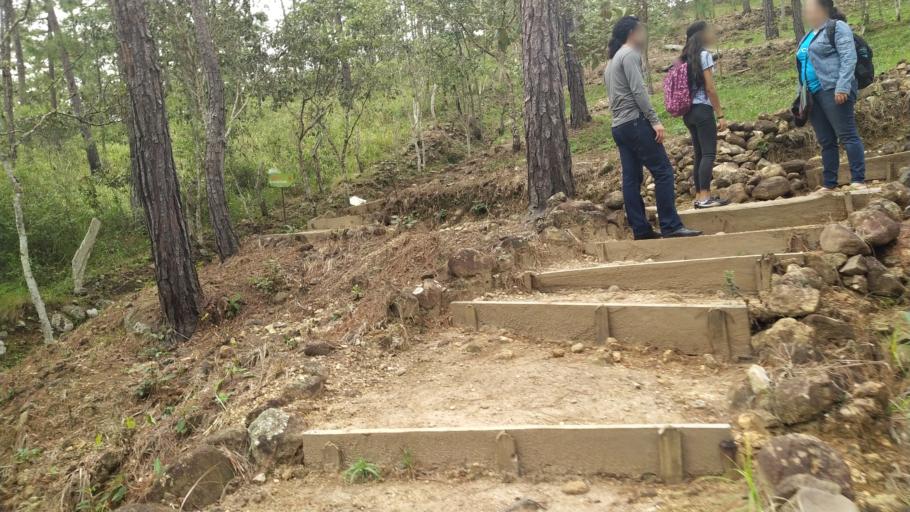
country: GT
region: Chiquimula
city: Esquipulas
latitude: 14.5548
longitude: -89.3194
